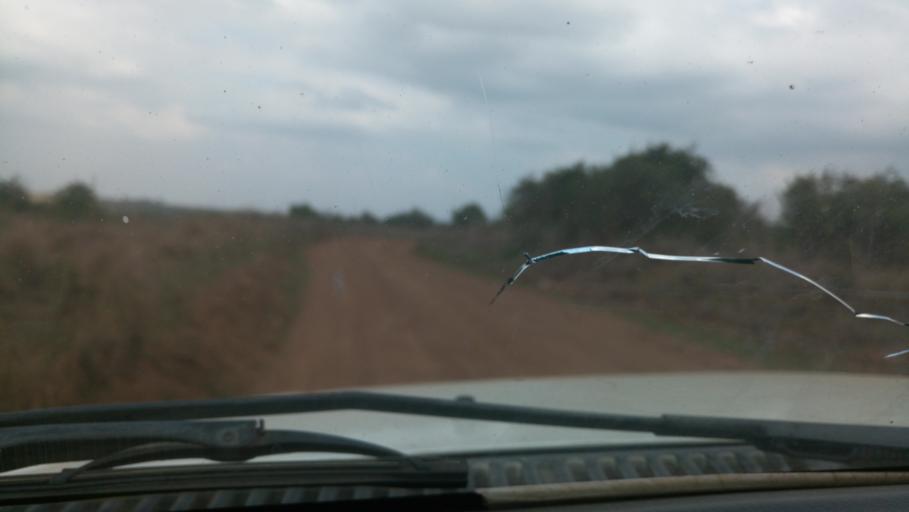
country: KE
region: Nairobi Area
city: Nairobi
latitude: -1.3678
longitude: 36.8328
